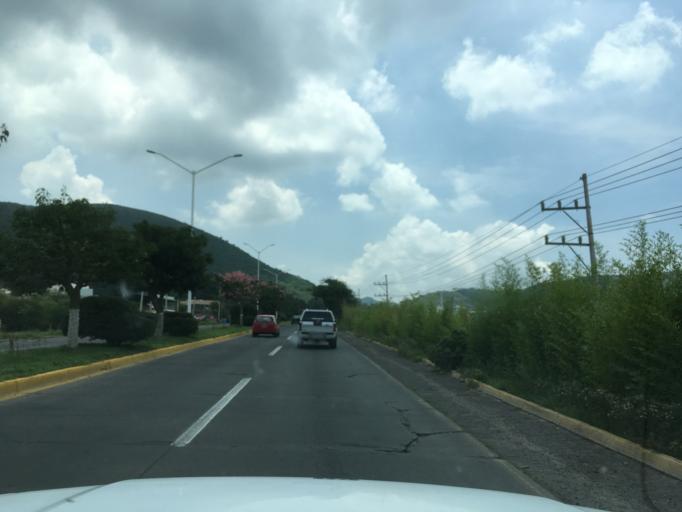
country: MX
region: Jalisco
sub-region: Tlajomulco de Zuniga
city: Santa Cruz de las Flores
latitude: 20.4905
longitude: -103.4781
